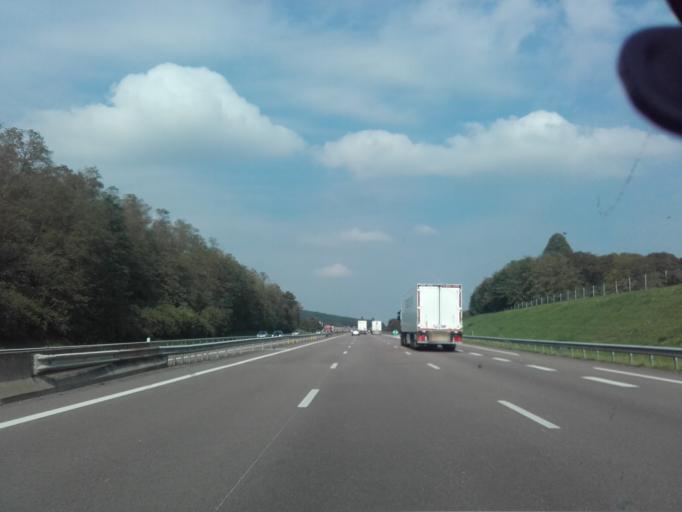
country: FR
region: Bourgogne
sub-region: Departement de Saone-et-Loire
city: Tournus
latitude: 46.5766
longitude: 4.8983
